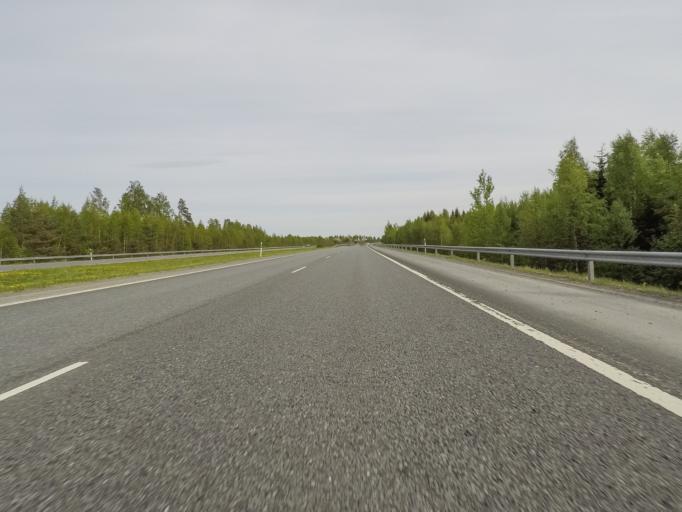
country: FI
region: Haeme
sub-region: Haemeenlinna
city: Kalvola
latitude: 61.1270
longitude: 24.1124
